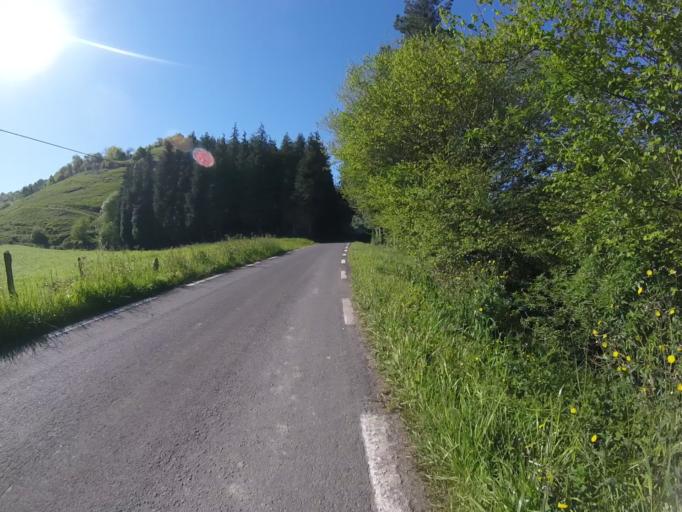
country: ES
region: Basque Country
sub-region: Provincia de Guipuzcoa
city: Aizarnazabal
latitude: 43.2269
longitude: -2.2141
